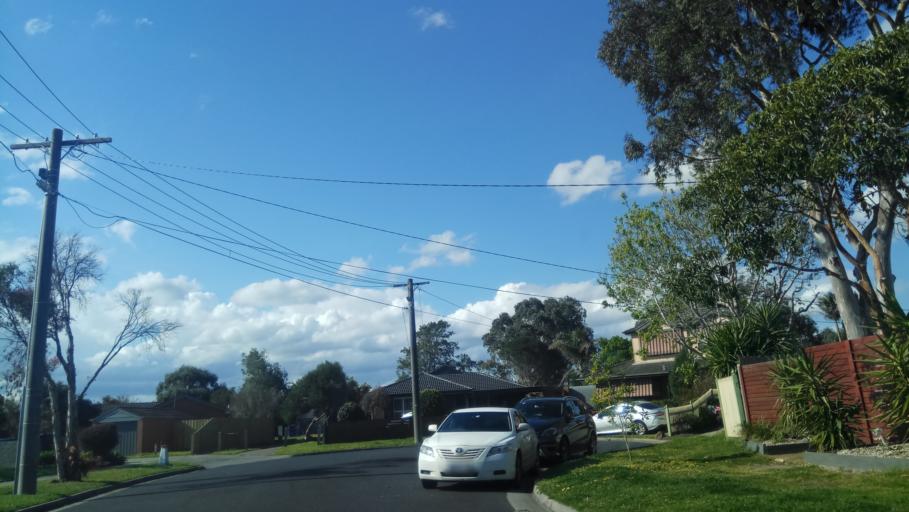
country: AU
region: Victoria
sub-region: Kingston
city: Dingley Village
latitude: -37.9869
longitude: 145.1246
